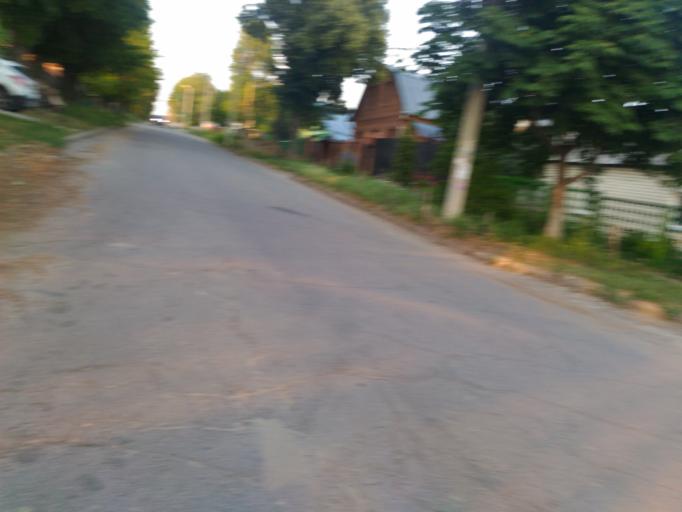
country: RU
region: Ulyanovsk
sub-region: Ulyanovskiy Rayon
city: Ulyanovsk
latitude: 54.3395
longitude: 48.3719
